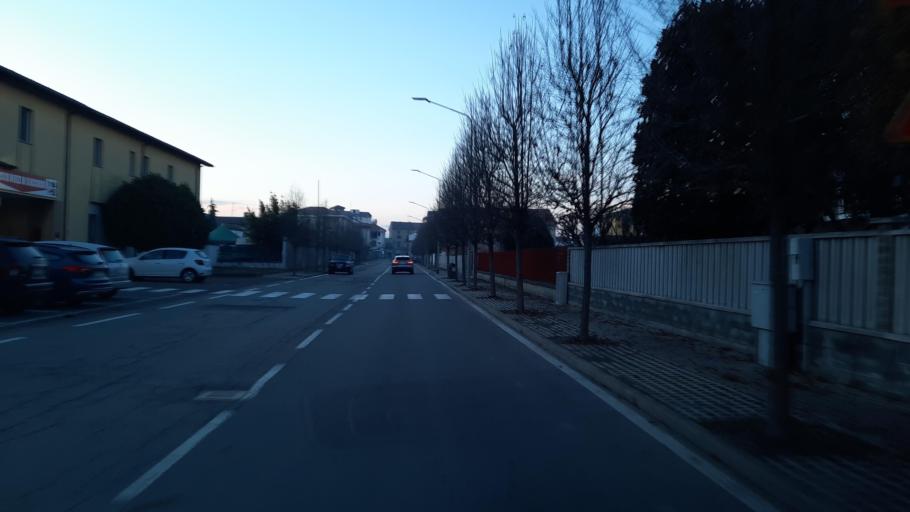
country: IT
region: Piedmont
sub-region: Provincia di Vercelli
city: Trino
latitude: 45.1958
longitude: 8.3008
